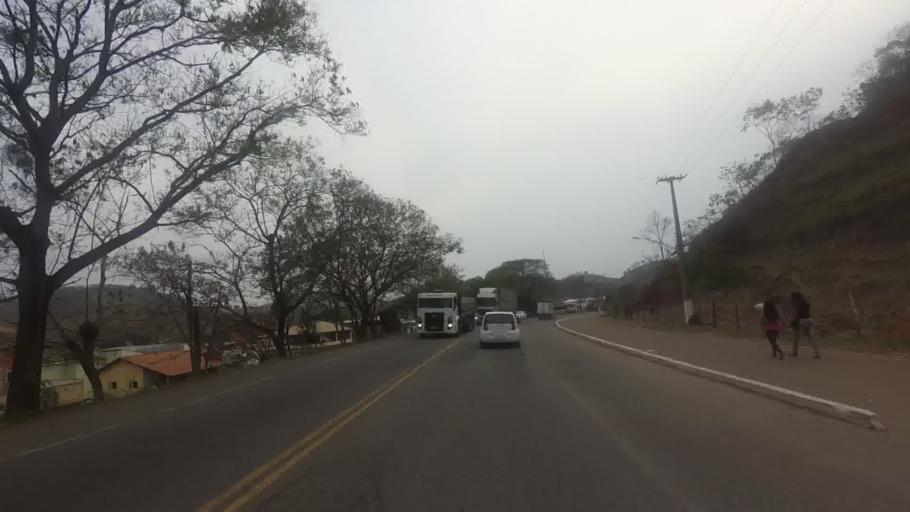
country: BR
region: Rio de Janeiro
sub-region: Santo Antonio De Padua
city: Santo Antonio de Padua
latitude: -21.5474
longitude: -42.1702
